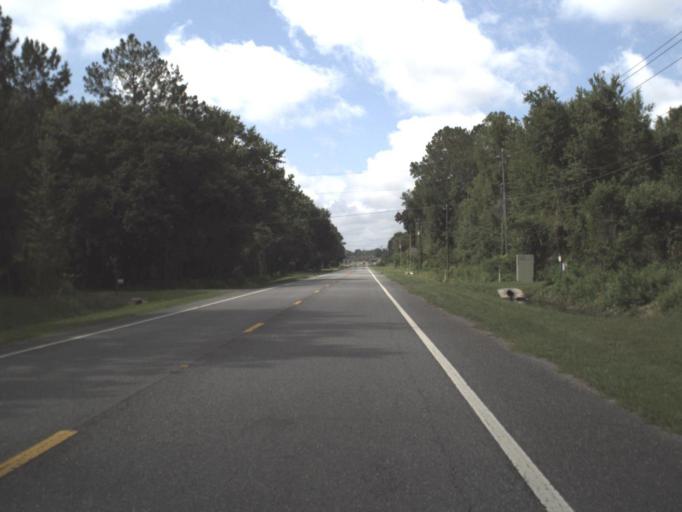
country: US
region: Florida
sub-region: Columbia County
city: Five Points
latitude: 30.2507
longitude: -82.6382
